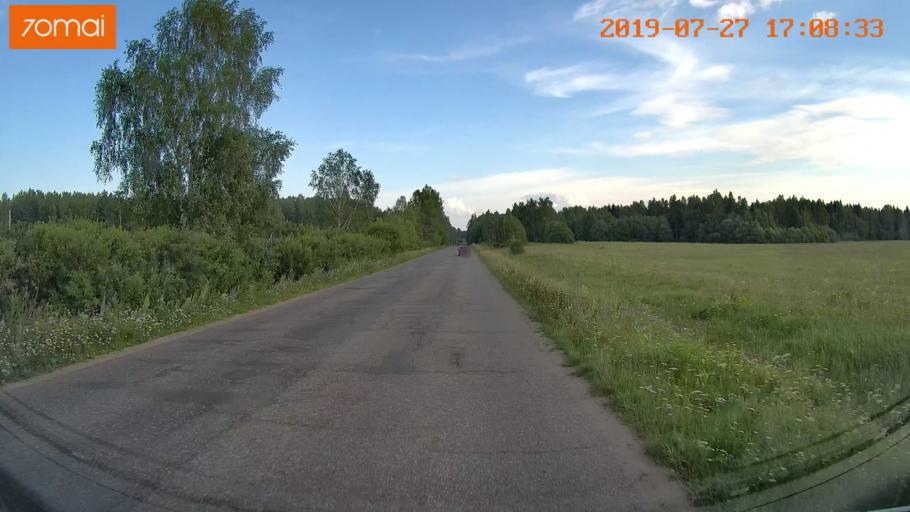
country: RU
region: Ivanovo
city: Novo-Talitsy
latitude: 57.0817
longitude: 40.8388
